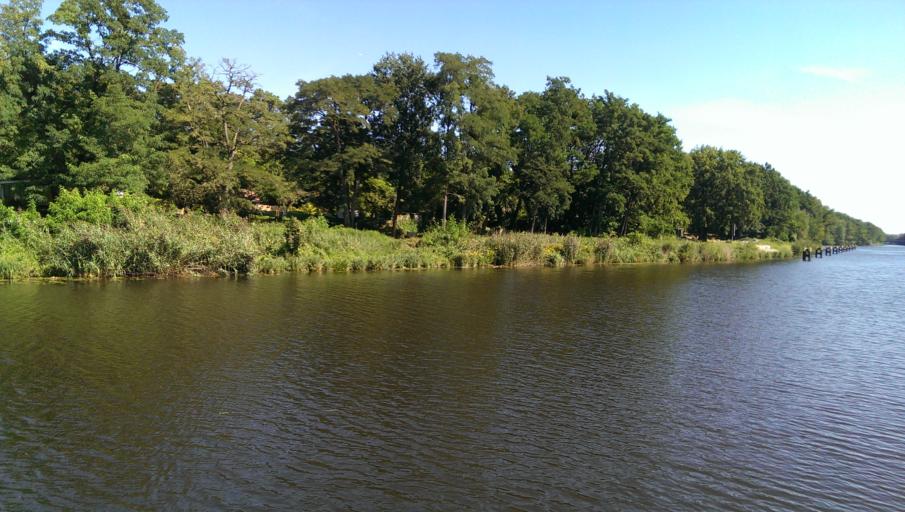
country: DE
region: Brandenburg
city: Stahnsdorf
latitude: 52.3960
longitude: 13.2114
